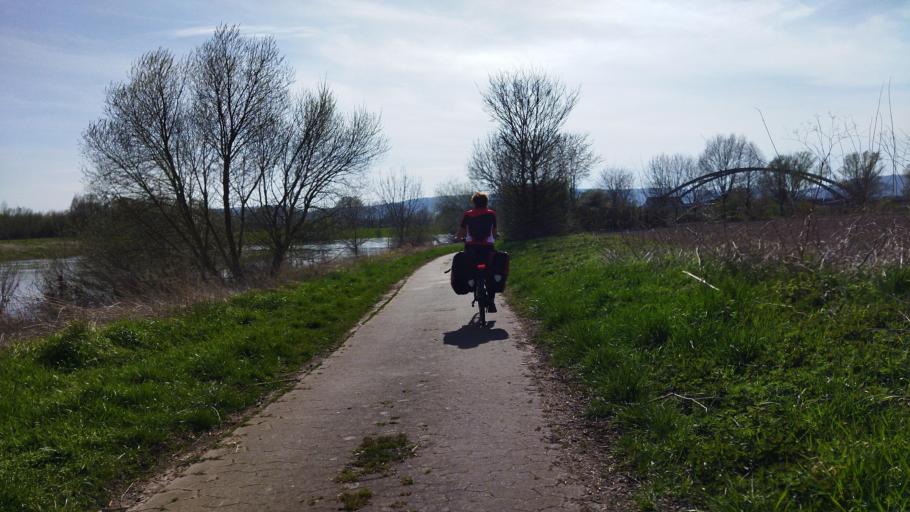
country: DE
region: Lower Saxony
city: Hessisch Oldendorf
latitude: 52.1595
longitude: 9.2540
